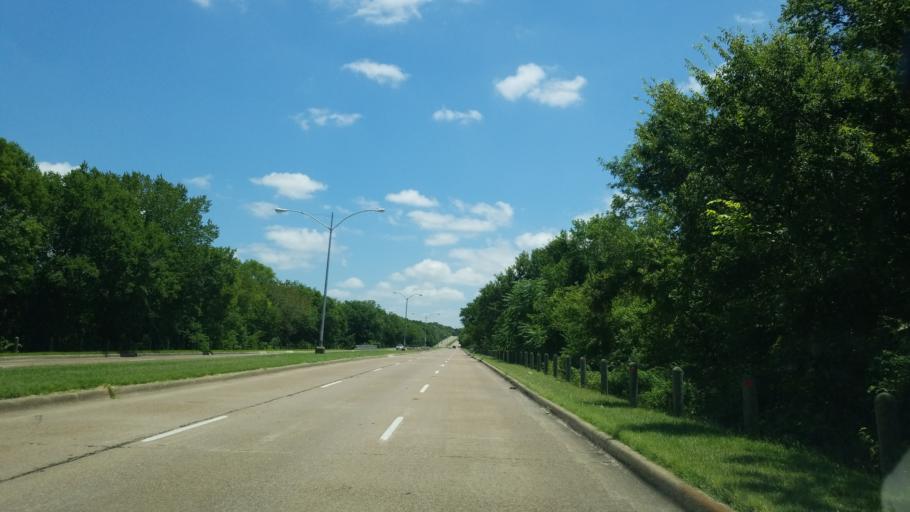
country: US
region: Texas
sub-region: Dallas County
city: Balch Springs
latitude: 32.7492
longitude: -96.7141
